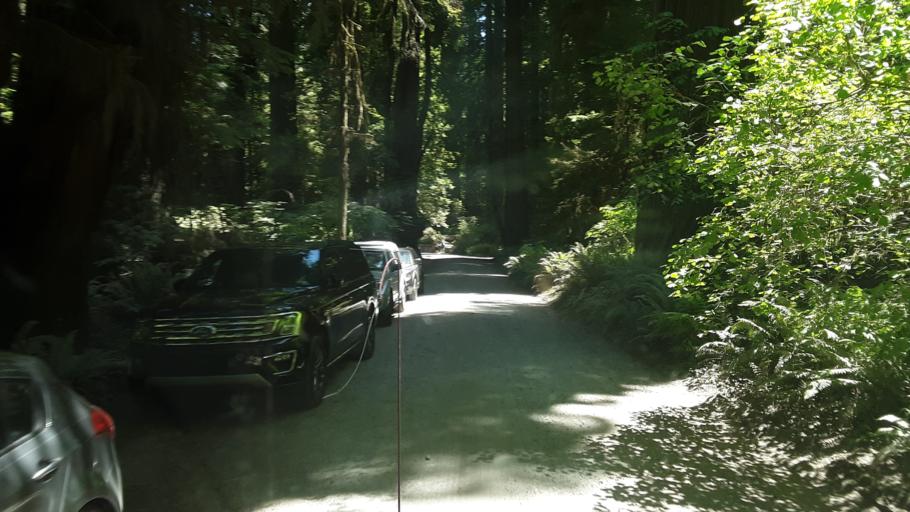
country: US
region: California
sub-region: Del Norte County
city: Bertsch-Oceanview
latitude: 41.8141
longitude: -124.1114
